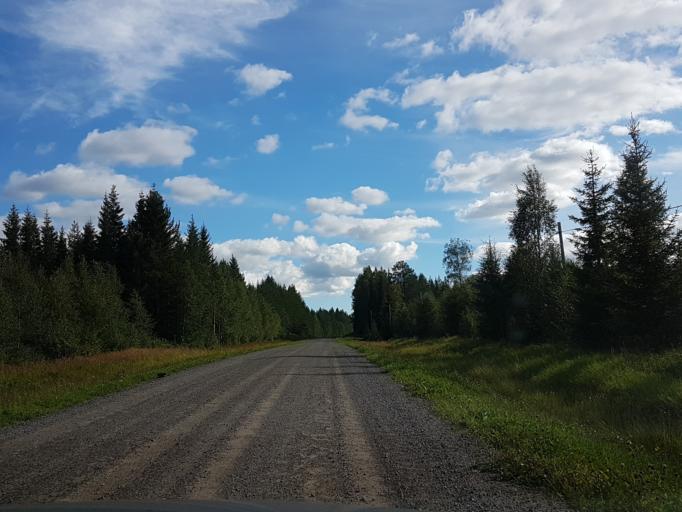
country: SE
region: Vaesterbotten
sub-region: Robertsfors Kommun
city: Robertsfors
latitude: 64.1786
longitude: 20.6451
